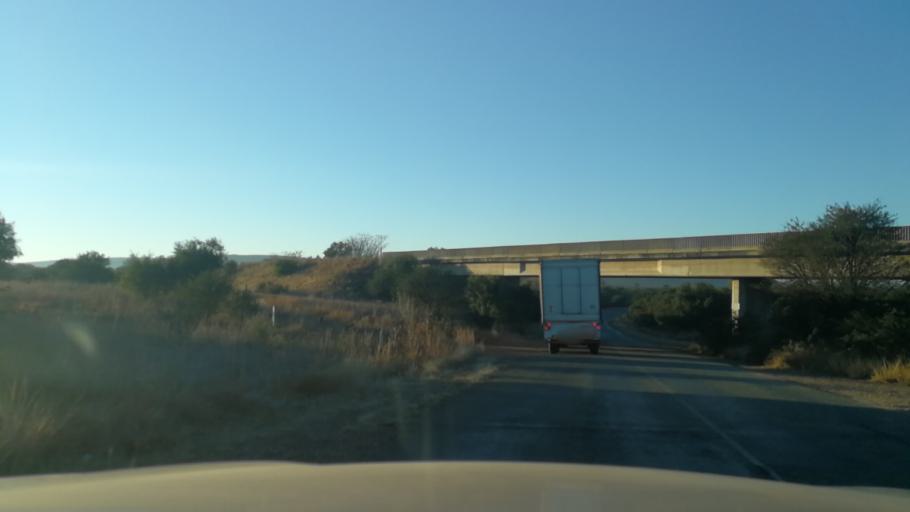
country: ZA
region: North-West
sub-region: Bojanala Platinum District Municipality
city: Koster
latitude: -25.6535
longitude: 26.7108
